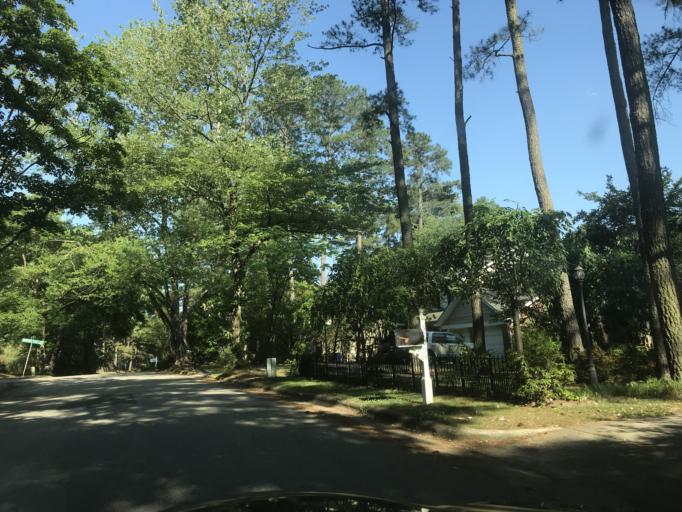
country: US
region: North Carolina
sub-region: Wake County
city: Raleigh
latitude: 35.8585
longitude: -78.6039
